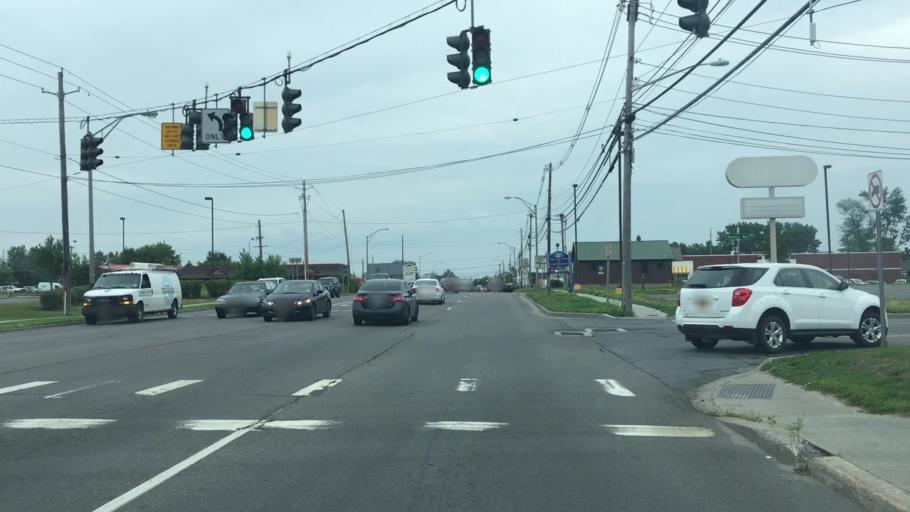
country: US
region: New York
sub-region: Clinton County
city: Plattsburgh West
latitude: 44.6970
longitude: -73.4834
